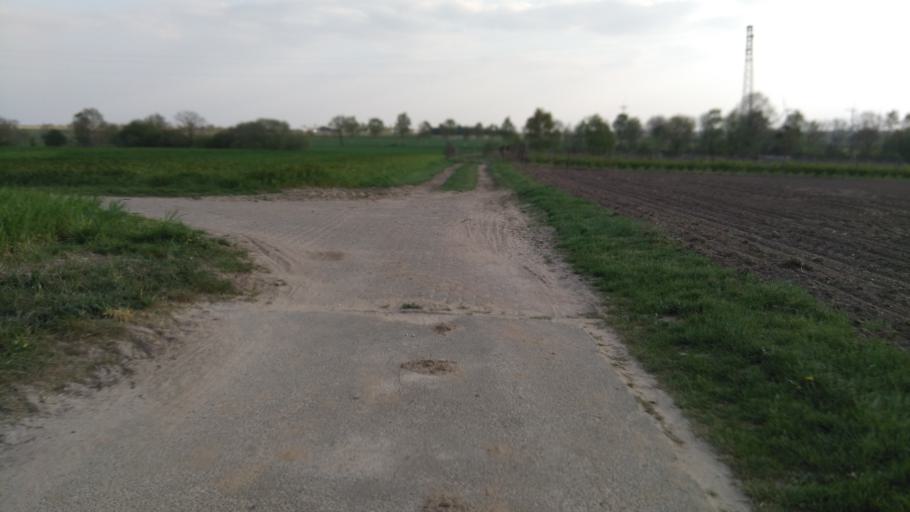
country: DE
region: Lower Saxony
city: Nottensdorf
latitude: 53.4689
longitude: 9.6260
